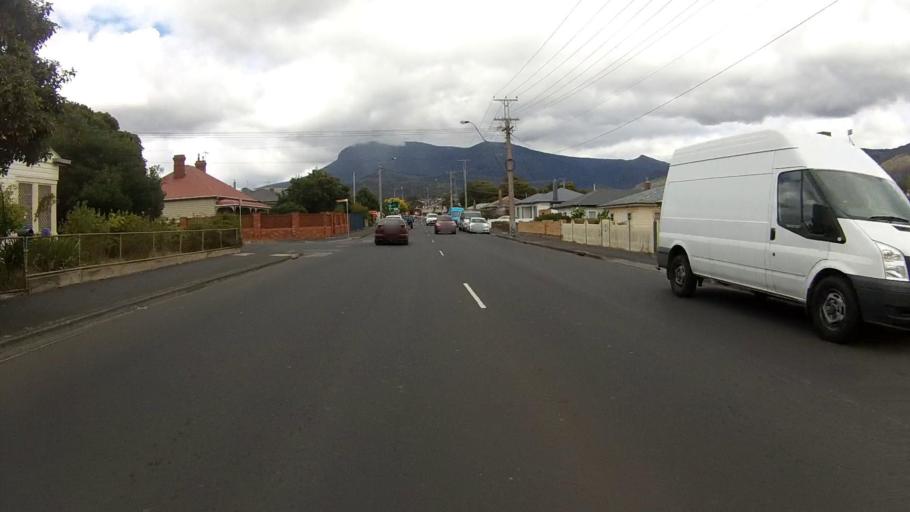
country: AU
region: Tasmania
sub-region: Glenorchy
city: Glenorchy
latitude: -42.8312
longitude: 147.2812
